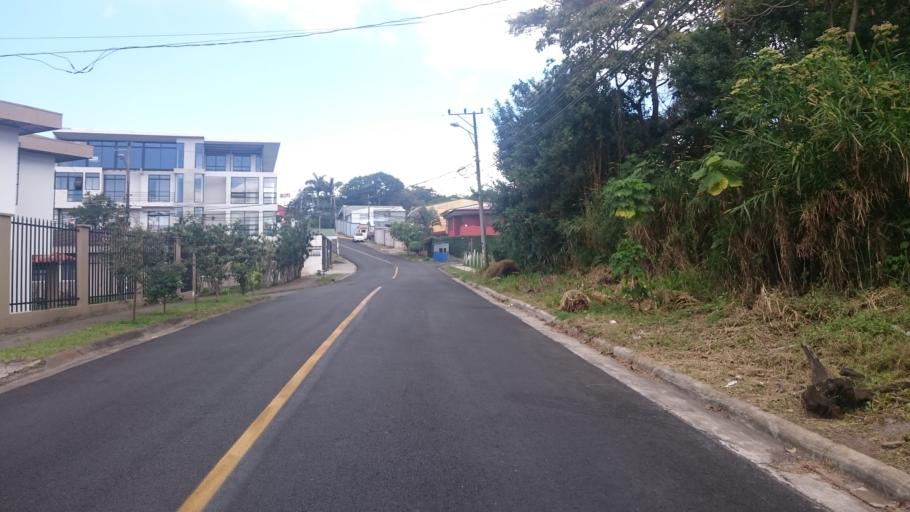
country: CR
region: San Jose
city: Curridabat
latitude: 9.9228
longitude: -84.0277
